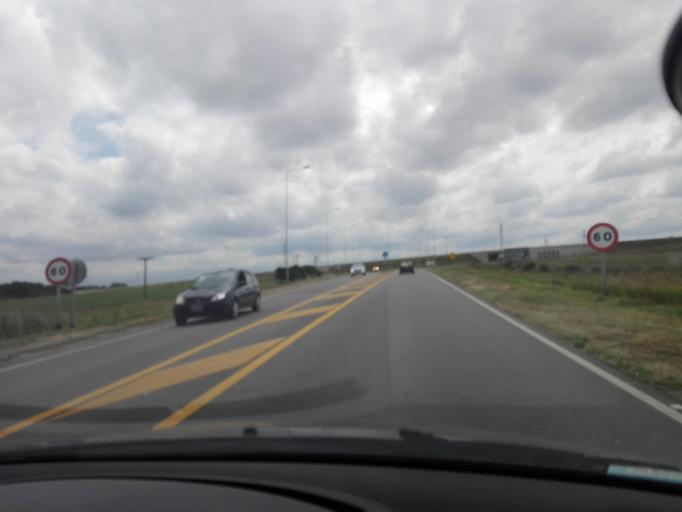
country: AR
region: Cordoba
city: Alta Gracia
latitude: -31.6521
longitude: -64.3114
